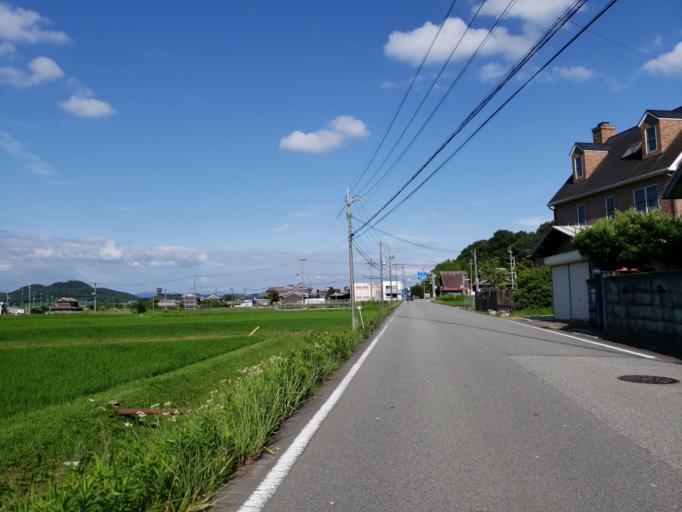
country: JP
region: Hyogo
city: Kakogawacho-honmachi
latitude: 34.8954
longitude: 134.8050
